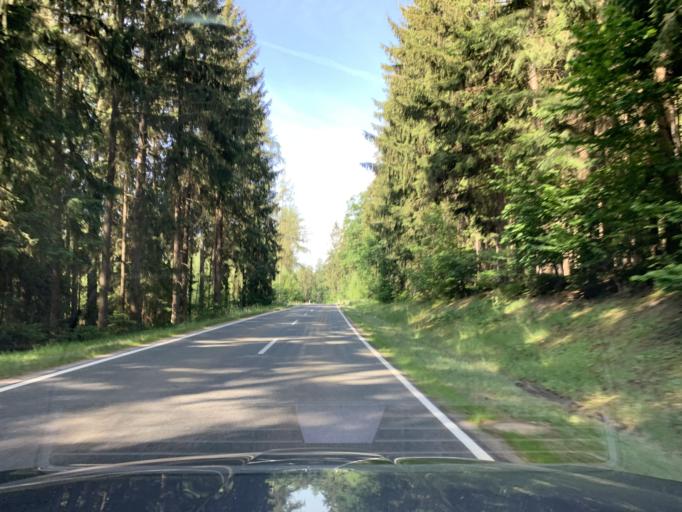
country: DE
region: Bavaria
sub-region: Upper Palatinate
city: Bach
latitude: 49.4143
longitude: 12.3726
